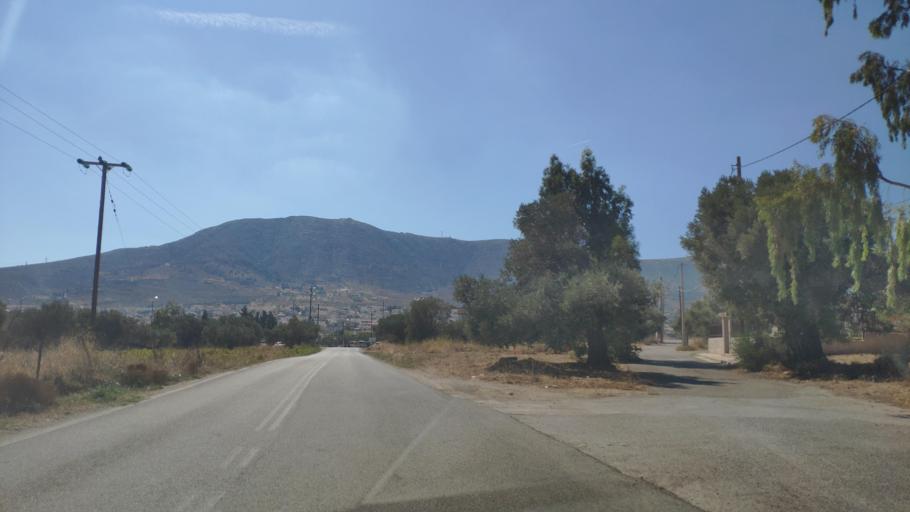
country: GR
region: Attica
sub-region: Nomarchia Anatolikis Attikis
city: Keratea
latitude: 37.8132
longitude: 23.9856
